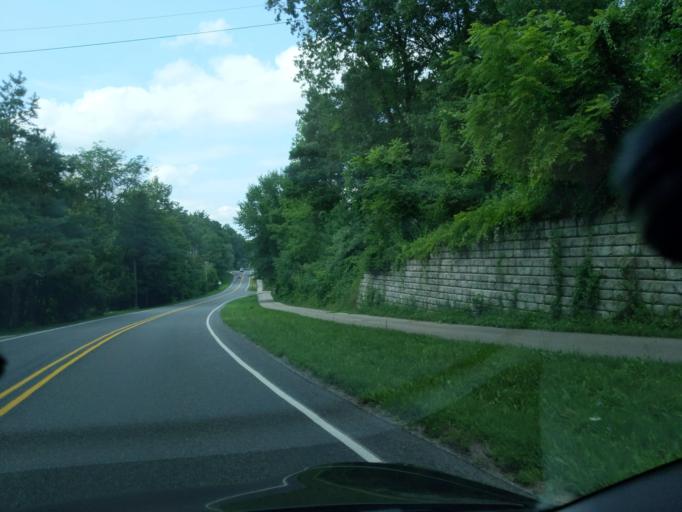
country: US
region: Michigan
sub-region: Kent County
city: Forest Hills
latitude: 42.9703
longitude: -85.5327
